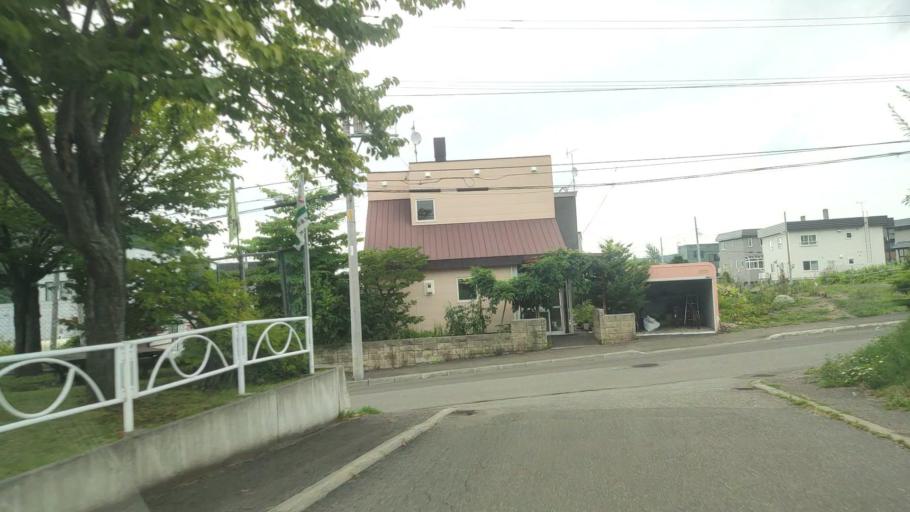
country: JP
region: Hokkaido
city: Sapporo
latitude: 42.9642
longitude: 141.3176
